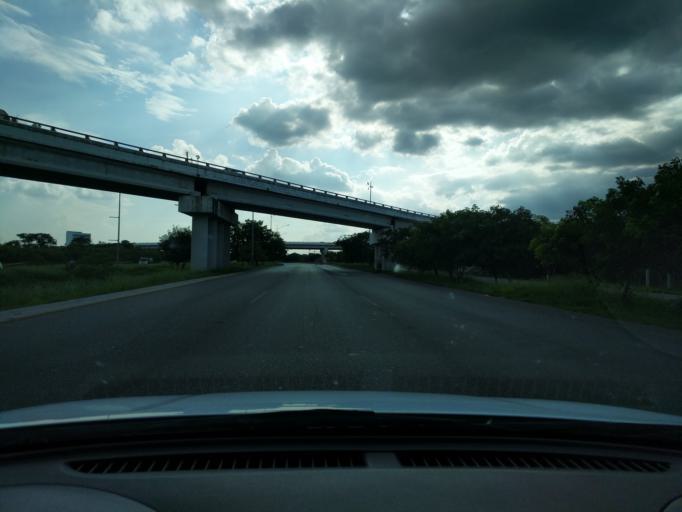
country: MX
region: Yucatan
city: Caucel
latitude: 20.9783
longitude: -89.6866
